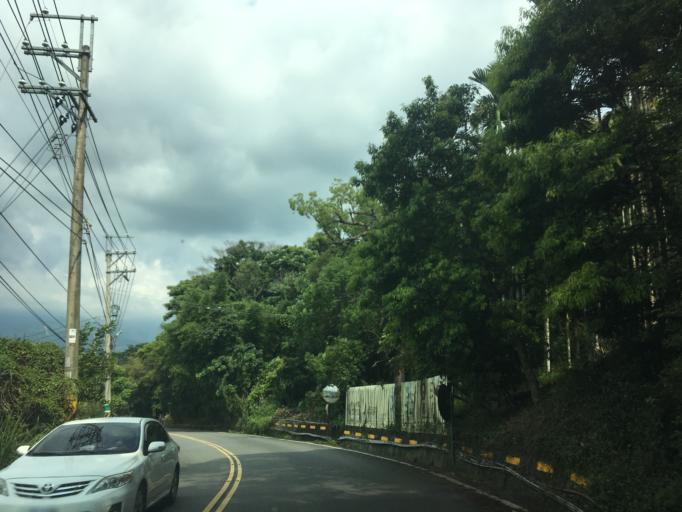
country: TW
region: Taiwan
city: Fengyuan
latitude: 24.2538
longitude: 120.8121
